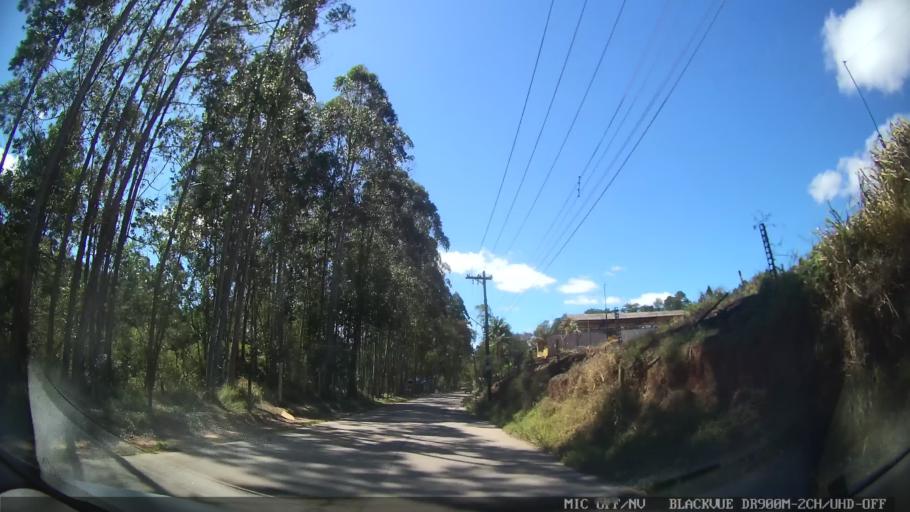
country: BR
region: Sao Paulo
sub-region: Campo Limpo Paulista
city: Campo Limpo Paulista
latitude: -23.1788
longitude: -46.7760
